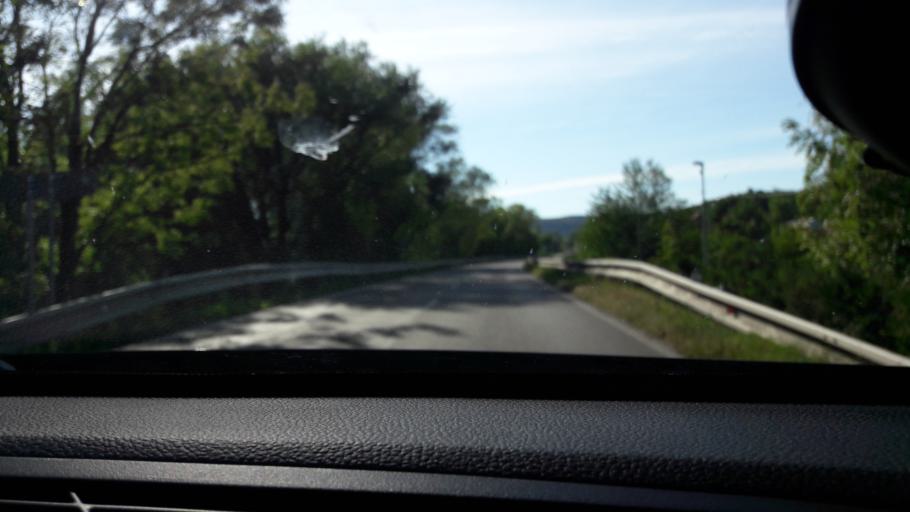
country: SK
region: Kosicky
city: Vinne
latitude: 48.8098
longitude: 22.0280
